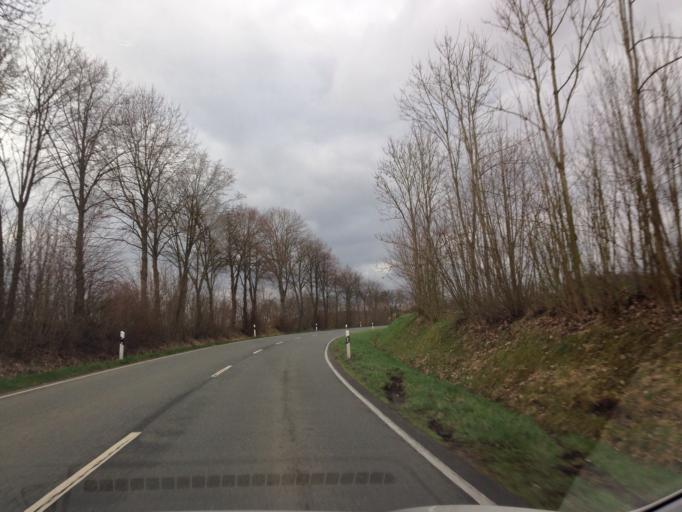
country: DE
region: North Rhine-Westphalia
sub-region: Regierungsbezirk Munster
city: Nordkirchen
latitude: 51.7583
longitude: 7.5243
